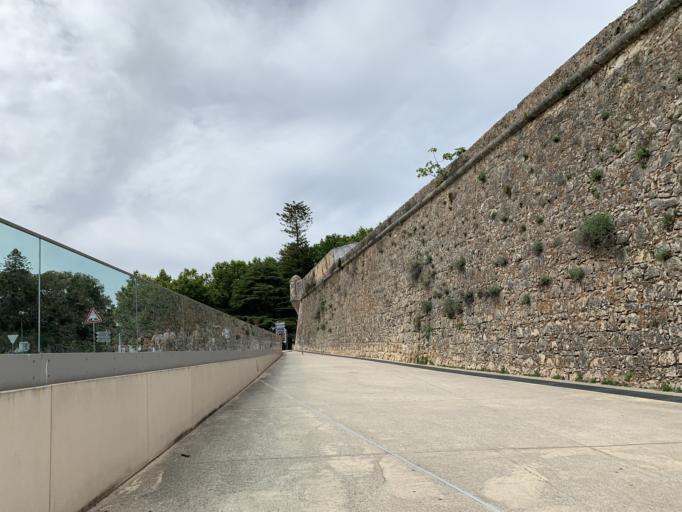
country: PT
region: Lisbon
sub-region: Cascais
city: Cascais
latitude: 38.6939
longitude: -9.4205
